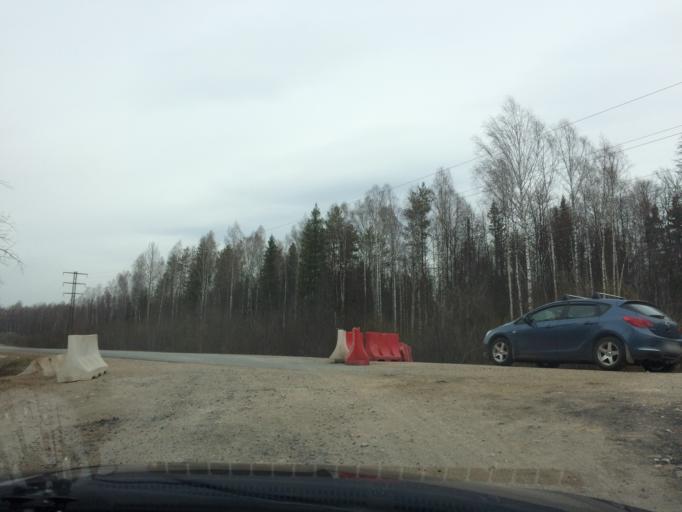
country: RU
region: Mariy-El
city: Surok
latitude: 56.5517
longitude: 48.3154
